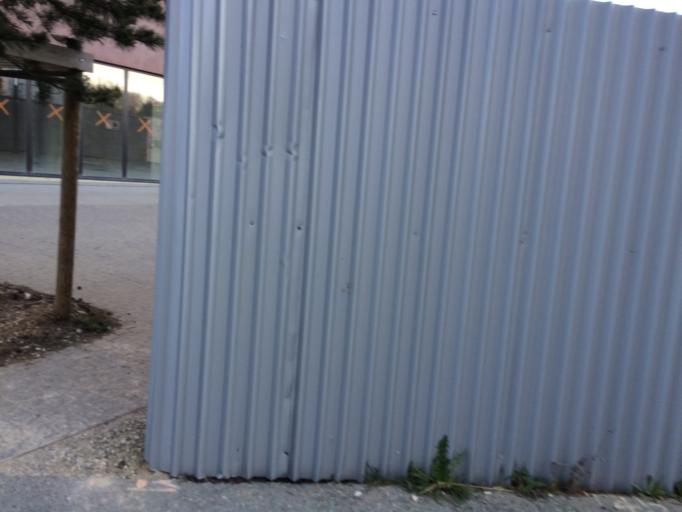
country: FR
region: Ile-de-France
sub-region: Departement de l'Essonne
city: Vauhallan
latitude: 48.7130
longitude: 2.2020
